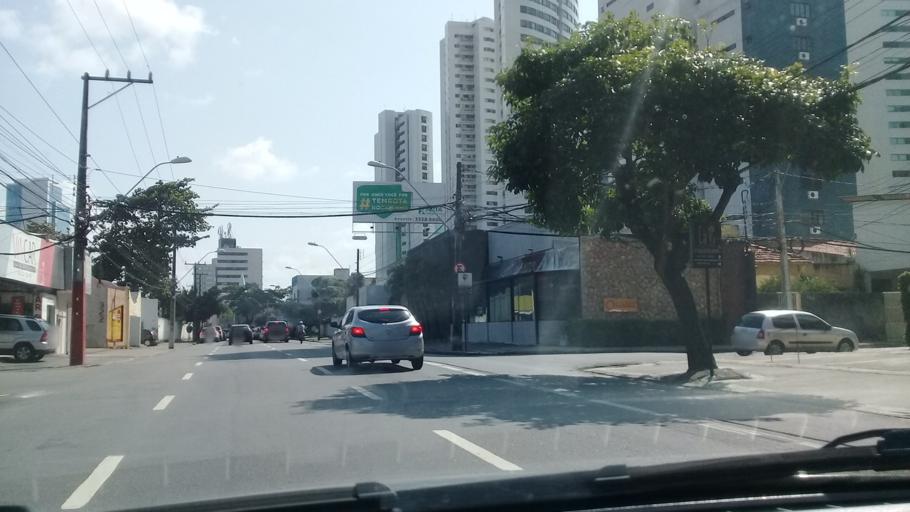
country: BR
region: Pernambuco
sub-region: Recife
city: Recife
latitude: -8.0941
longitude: -34.8842
